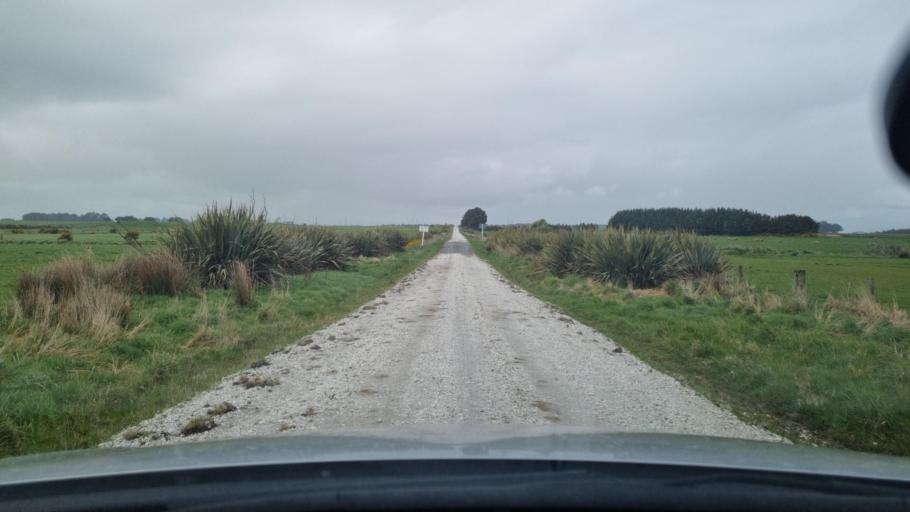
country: NZ
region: Southland
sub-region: Invercargill City
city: Invercargill
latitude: -46.5036
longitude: 168.4016
